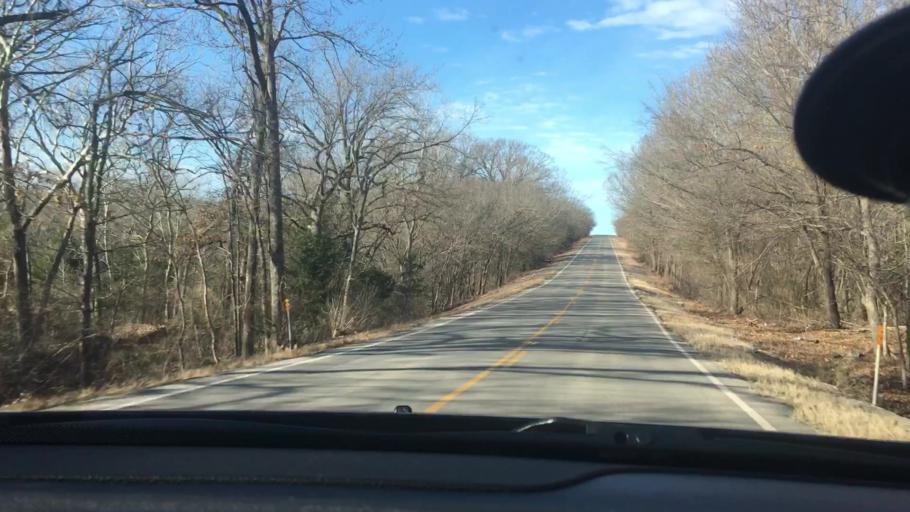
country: US
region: Oklahoma
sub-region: Seminole County
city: Konawa
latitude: 34.9856
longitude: -96.8341
